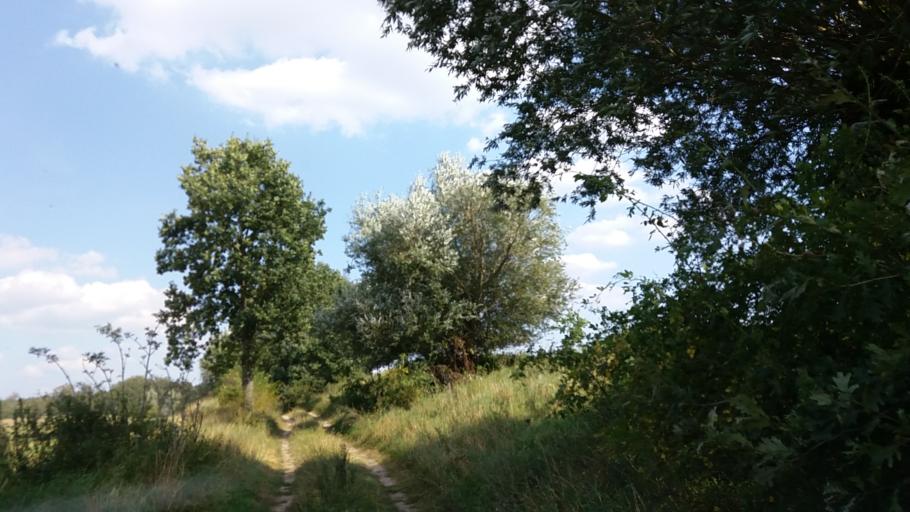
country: PL
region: West Pomeranian Voivodeship
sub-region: Powiat choszczenski
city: Krzecin
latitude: 53.1029
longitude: 15.4301
